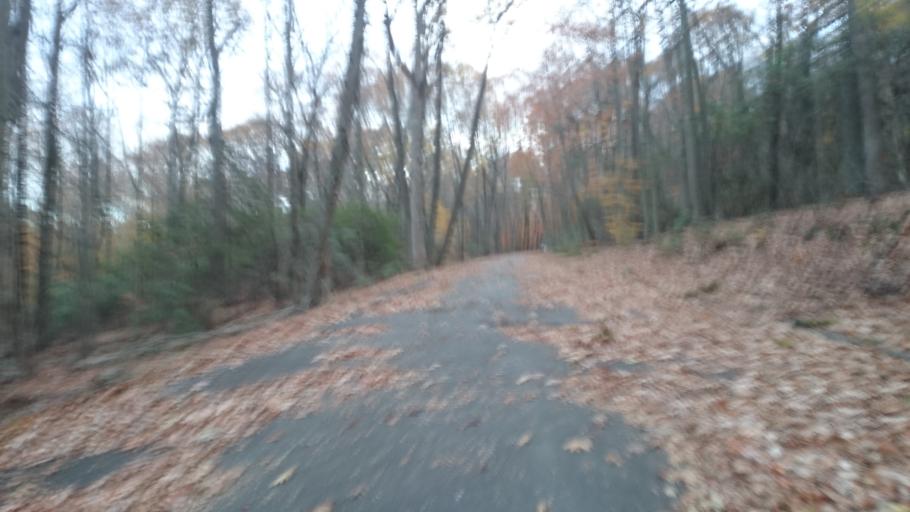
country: US
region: Connecticut
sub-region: New Haven County
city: Woodbridge
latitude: 41.3440
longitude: -72.9664
